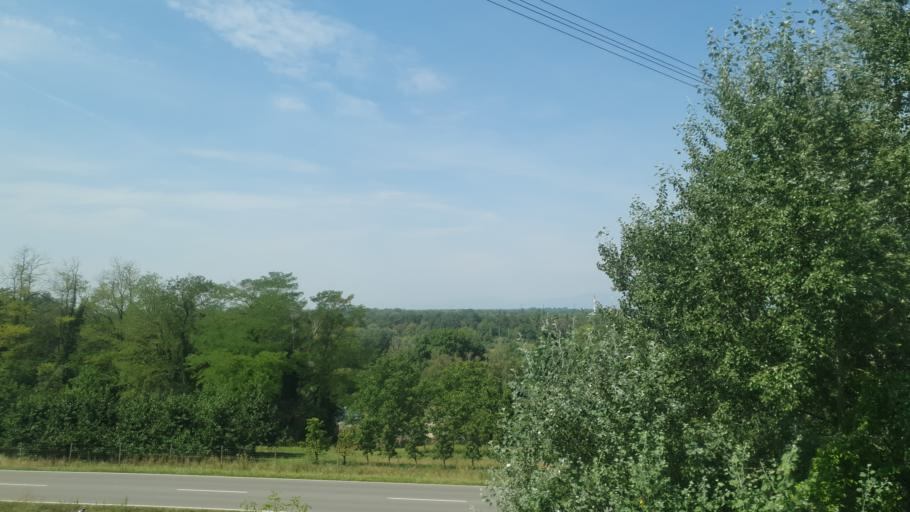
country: DE
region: Baden-Wuerttemberg
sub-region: Freiburg Region
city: Bad Bellingen
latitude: 47.7465
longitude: 7.5607
